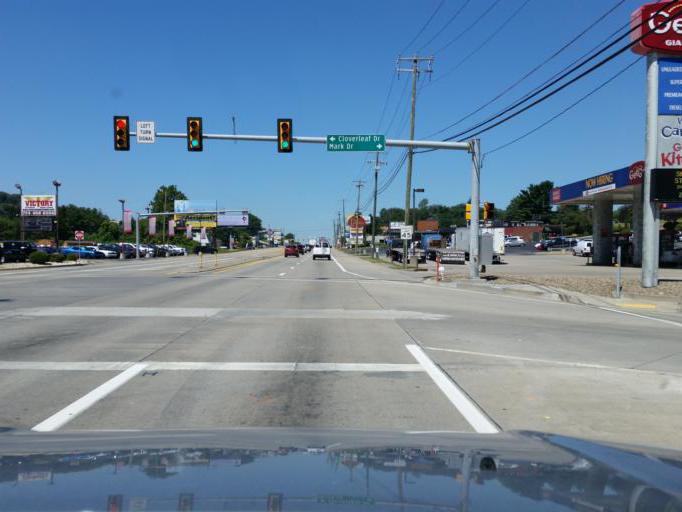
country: US
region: Pennsylvania
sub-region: Westmoreland County
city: Delmont
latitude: 40.3992
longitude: -79.5793
